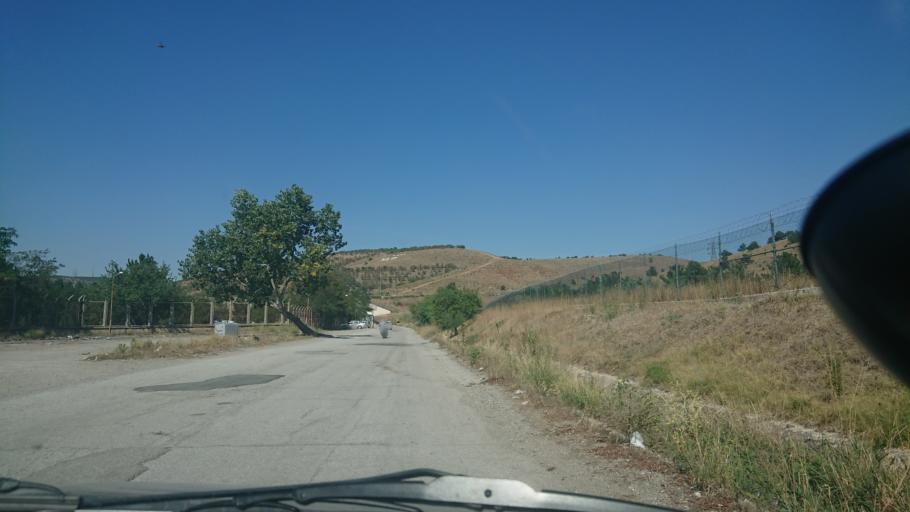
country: TR
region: Ankara
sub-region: Goelbasi
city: Golbasi
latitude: 39.8104
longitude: 32.8209
